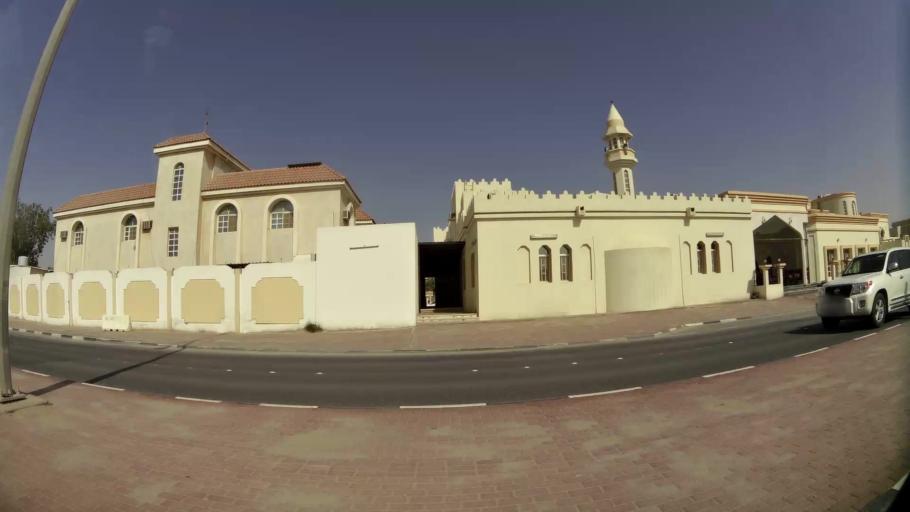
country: QA
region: Baladiyat Umm Salal
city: Umm Salal Muhammad
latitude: 25.3671
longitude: 51.4355
